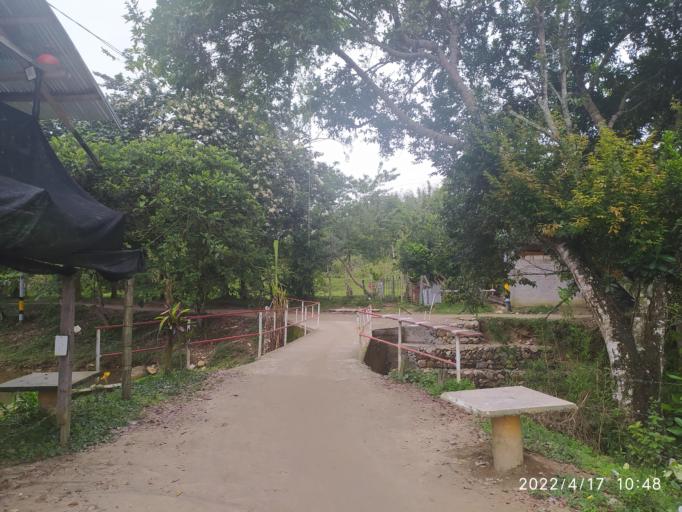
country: CO
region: Antioquia
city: San Carlos
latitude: 6.1845
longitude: -74.9904
